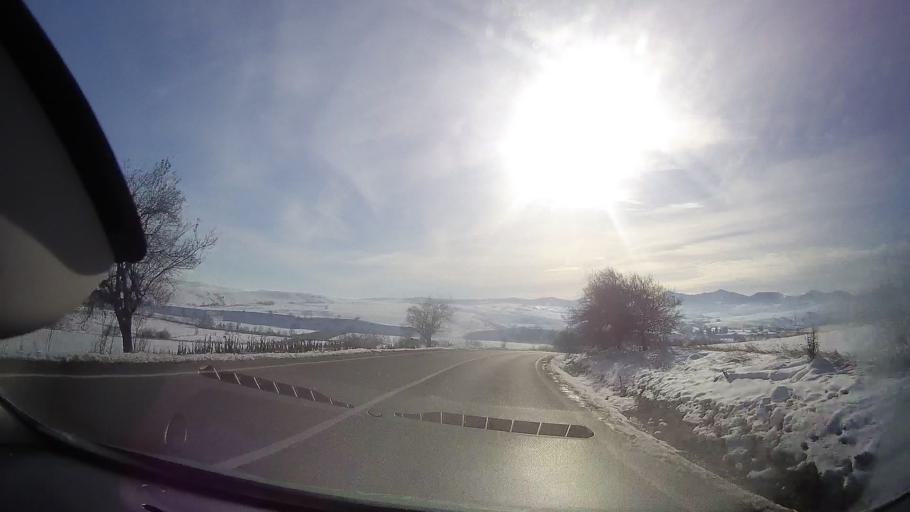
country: RO
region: Neamt
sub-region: Comuna Baltatesti
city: Valea Seaca
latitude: 47.1497
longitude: 26.3244
